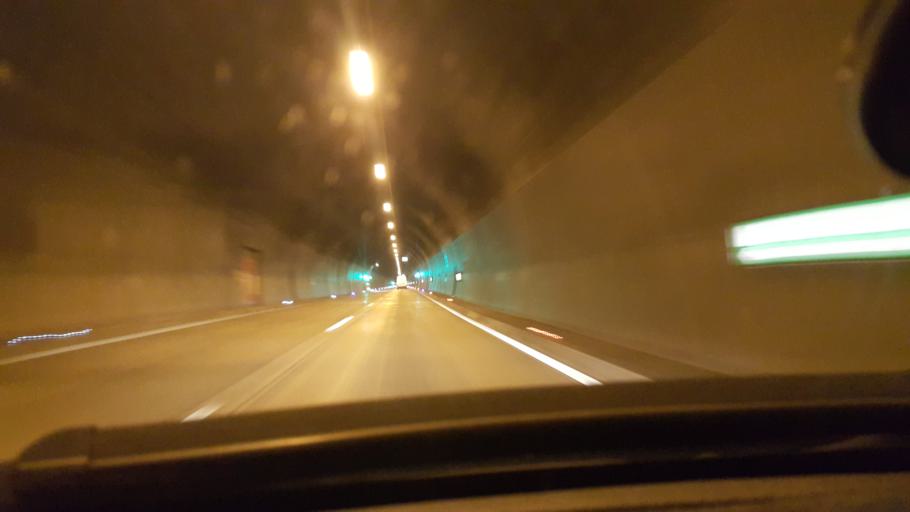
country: SI
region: Zagorje ob Savi
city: Izlake
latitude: 46.1833
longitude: 14.8581
